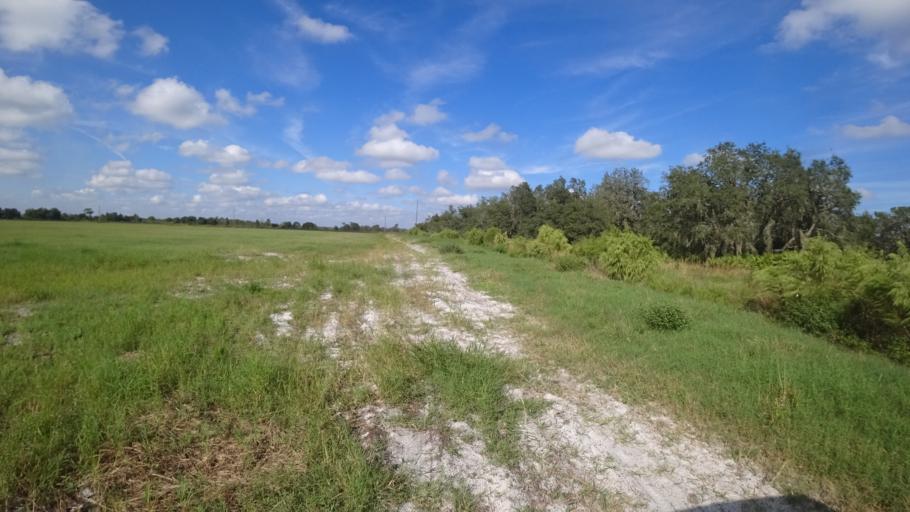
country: US
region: Florida
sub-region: Sarasota County
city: Lake Sarasota
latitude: 27.3714
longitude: -82.1676
